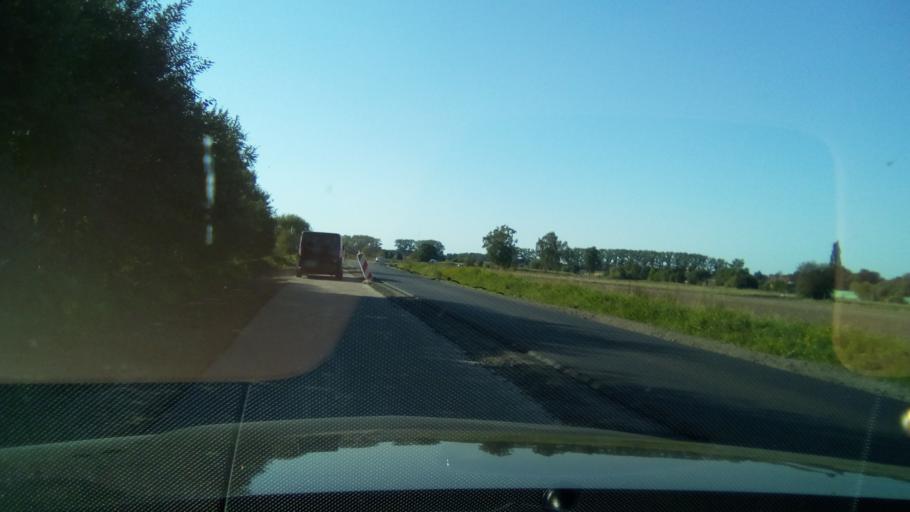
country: PL
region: West Pomeranian Voivodeship
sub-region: Powiat gryficki
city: Ploty
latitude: 53.8132
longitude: 15.1770
